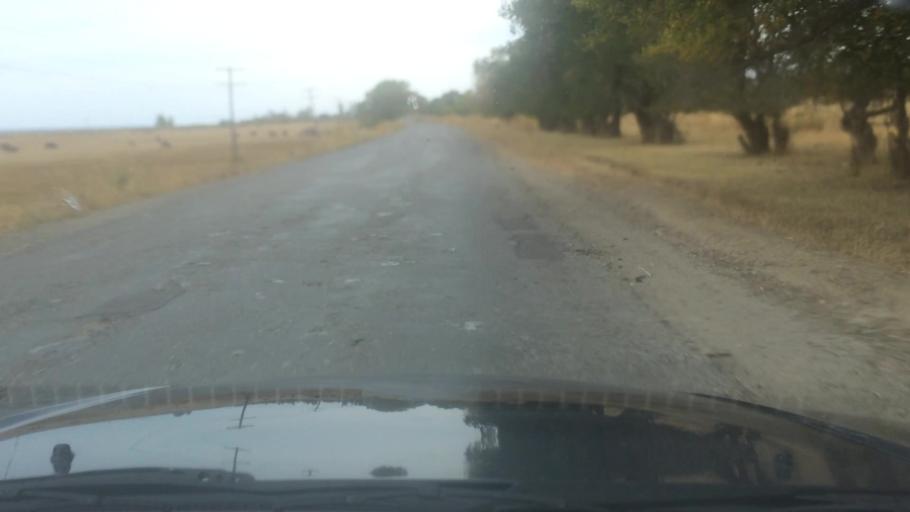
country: KG
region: Ysyk-Koel
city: Balykchy
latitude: 42.3079
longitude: 76.4657
